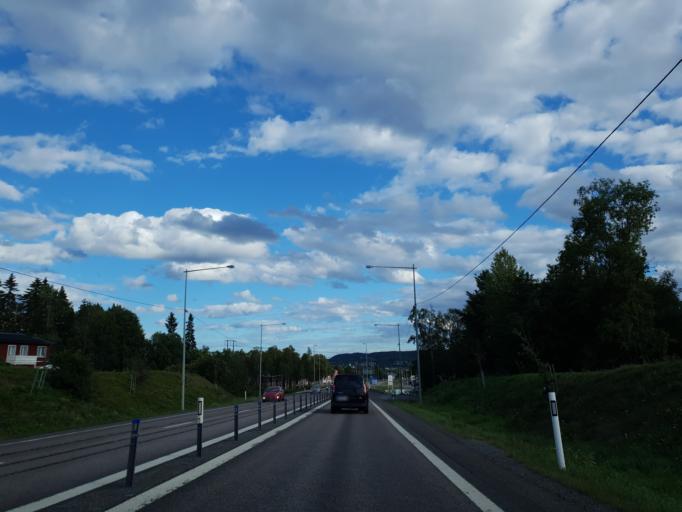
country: SE
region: Vaesternorrland
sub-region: Haernoesands Kommun
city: Haernoesand
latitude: 62.6451
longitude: 17.9053
